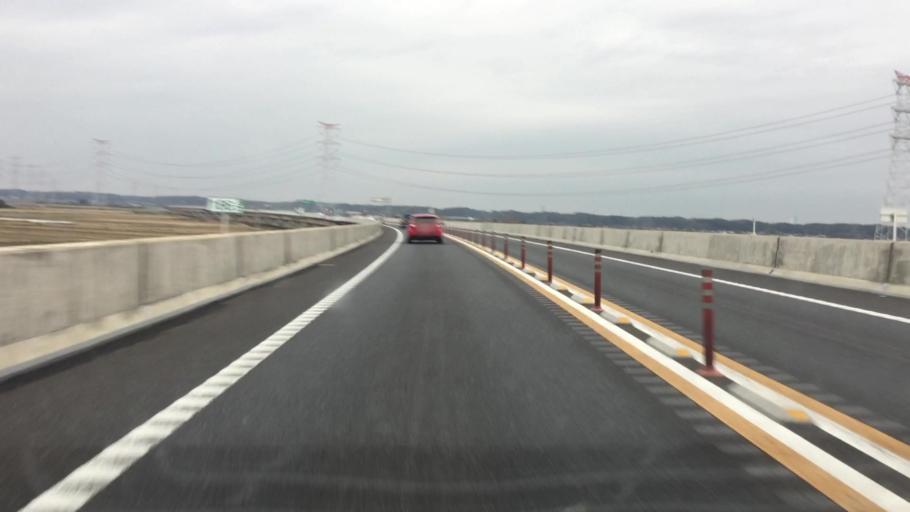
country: JP
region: Ibaraki
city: Inashiki
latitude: 35.9103
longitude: 140.3695
